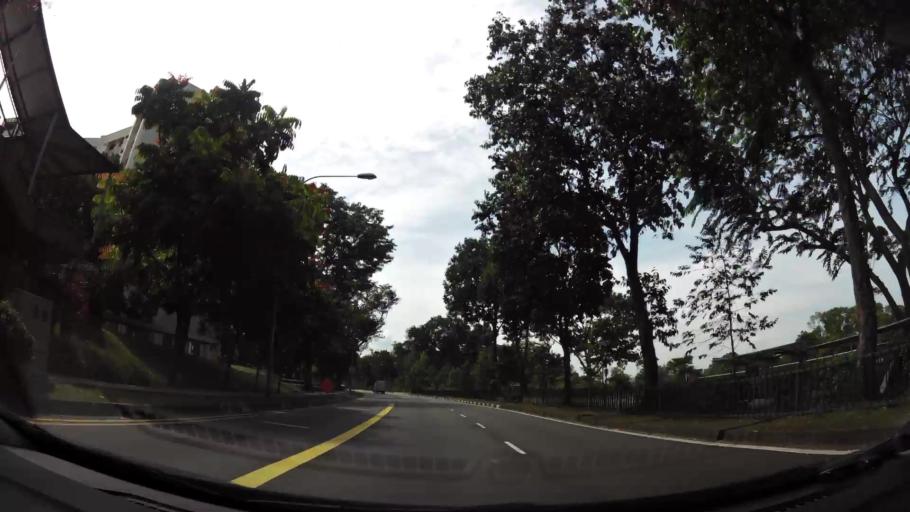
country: SG
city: Singapore
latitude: 1.3393
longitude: 103.7341
